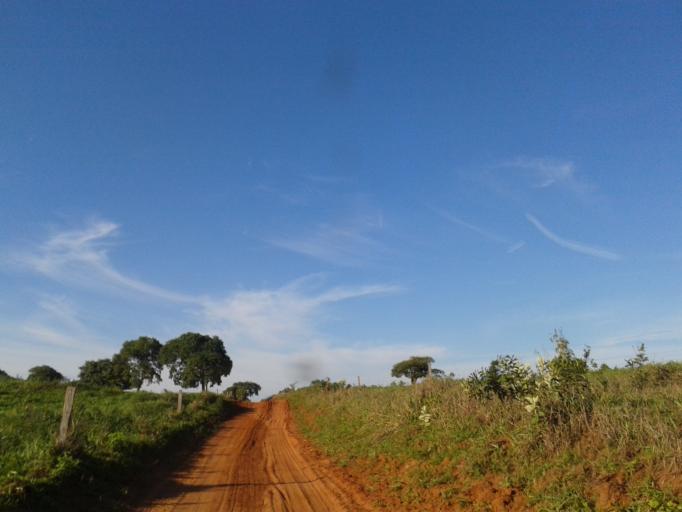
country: BR
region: Minas Gerais
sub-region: Santa Vitoria
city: Santa Vitoria
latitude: -18.9764
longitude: -49.8905
